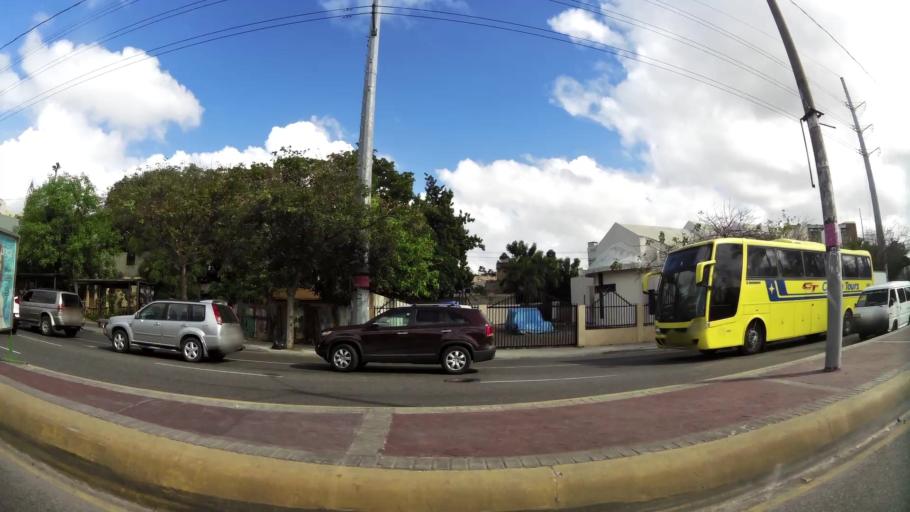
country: DO
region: Nacional
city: San Carlos
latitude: 18.4768
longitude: -69.8929
